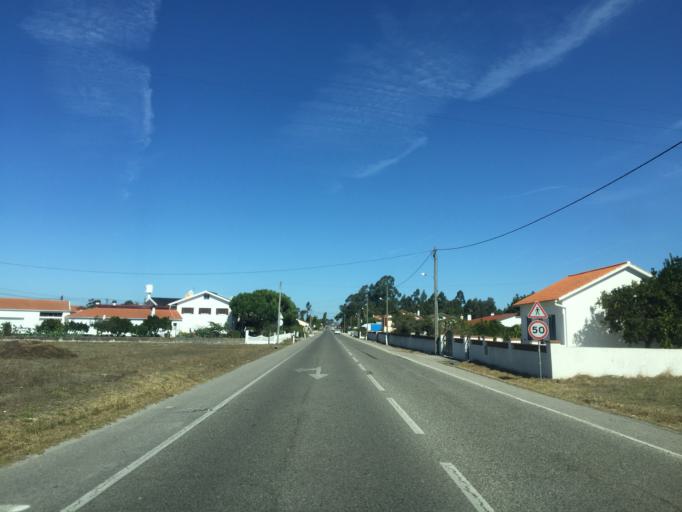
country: PT
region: Coimbra
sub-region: Figueira da Foz
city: Alhadas
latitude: 40.2436
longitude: -8.7901
